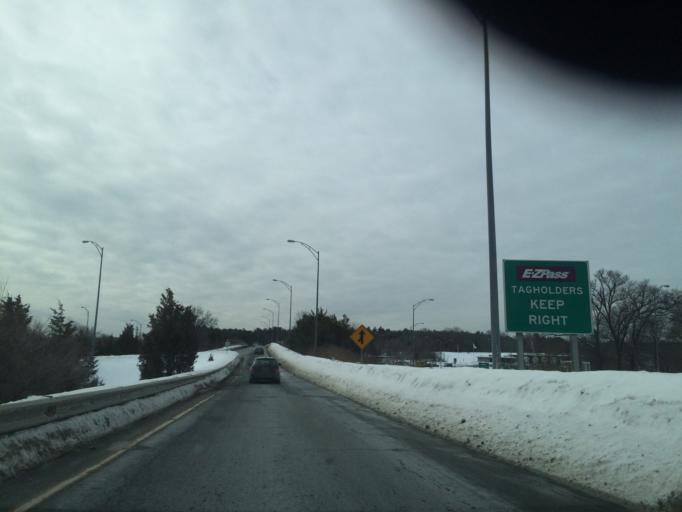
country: US
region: Massachusetts
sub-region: Middlesex County
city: Waltham
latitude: 42.3424
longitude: -71.2650
